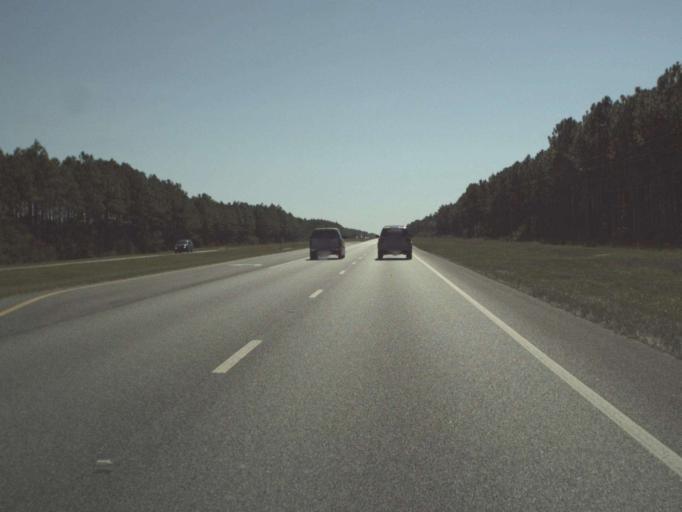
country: US
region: Florida
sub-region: Walton County
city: Seaside
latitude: 30.3163
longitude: -86.0427
